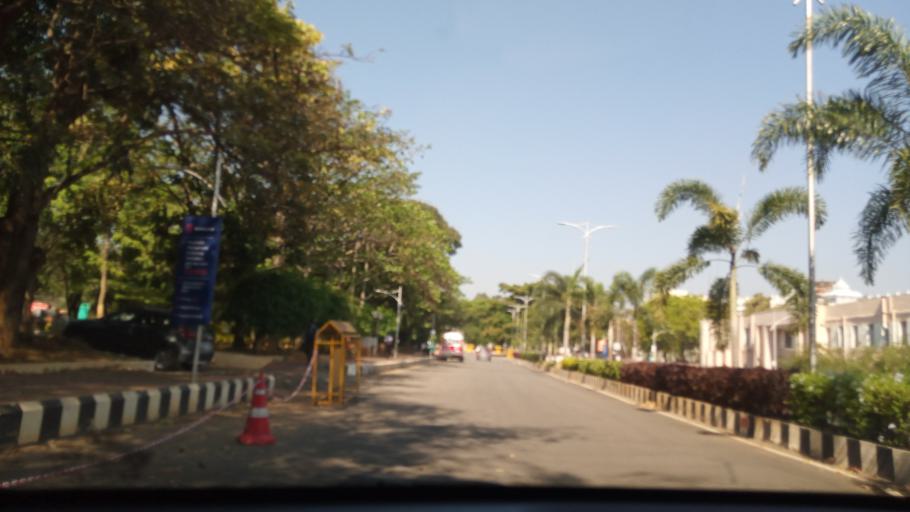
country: IN
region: Karnataka
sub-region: Bangalore Urban
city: Bangalore
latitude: 13.0288
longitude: 77.5677
